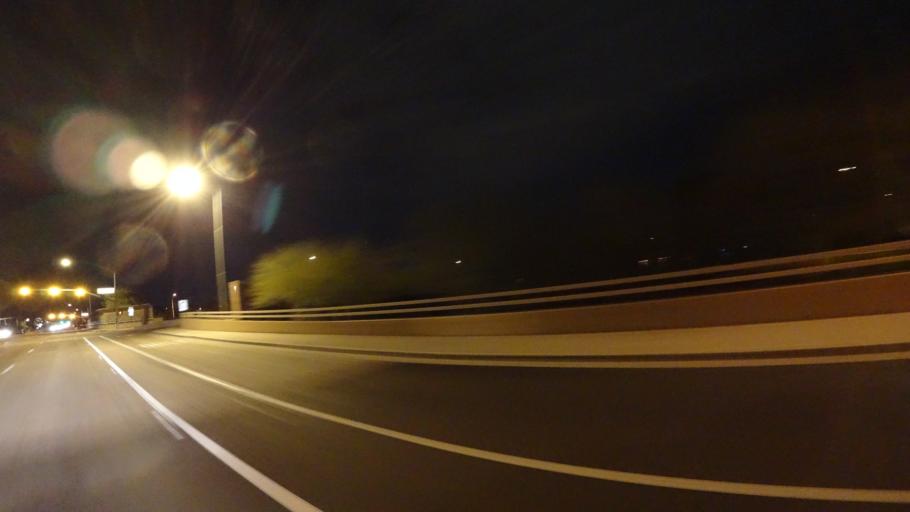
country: US
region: Arizona
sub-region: Maricopa County
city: Chandler
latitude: 33.2860
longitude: -111.8761
